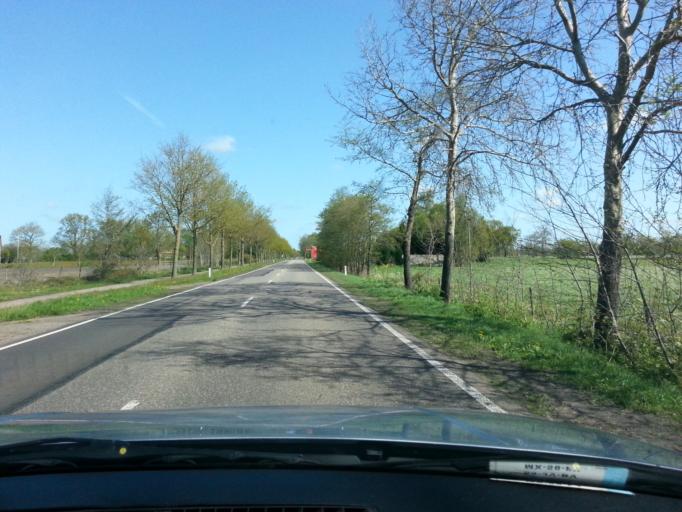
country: NL
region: Friesland
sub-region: Gemeente Smallingerland
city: Drachtstercompagnie
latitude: 53.1364
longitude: 6.1751
